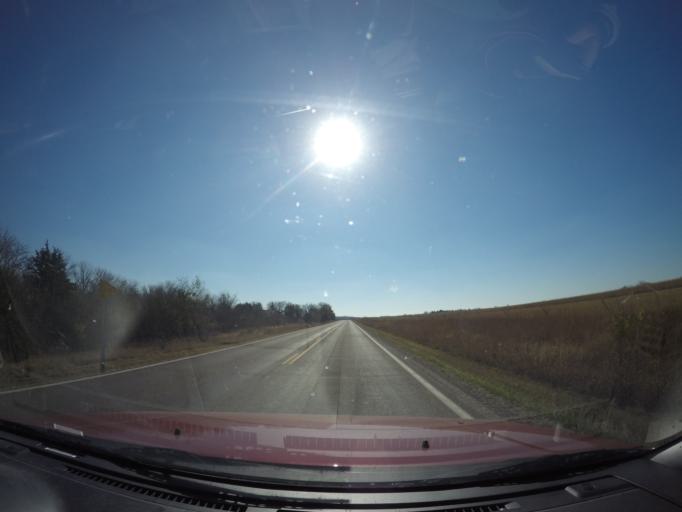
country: US
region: Kansas
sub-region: Morris County
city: Council Grove
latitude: 38.7454
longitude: -96.5012
